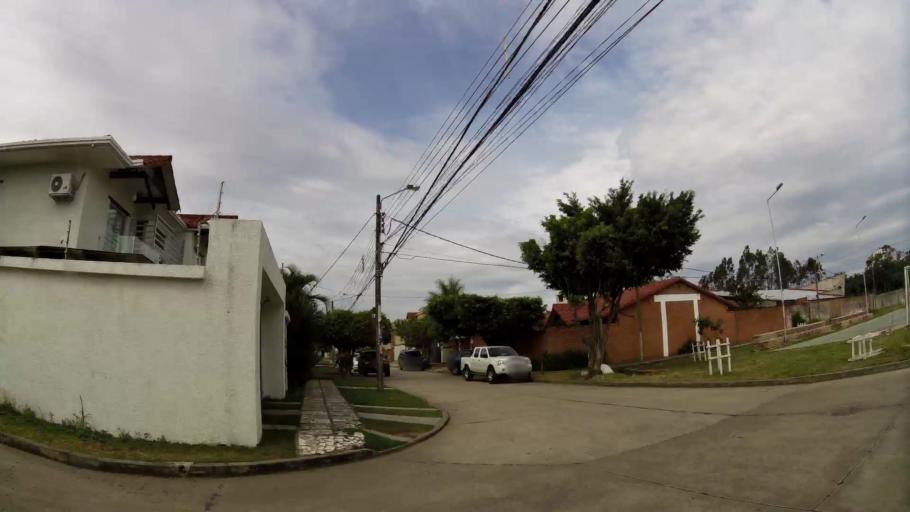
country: BO
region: Santa Cruz
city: Santa Cruz de la Sierra
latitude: -17.7822
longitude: -63.2136
